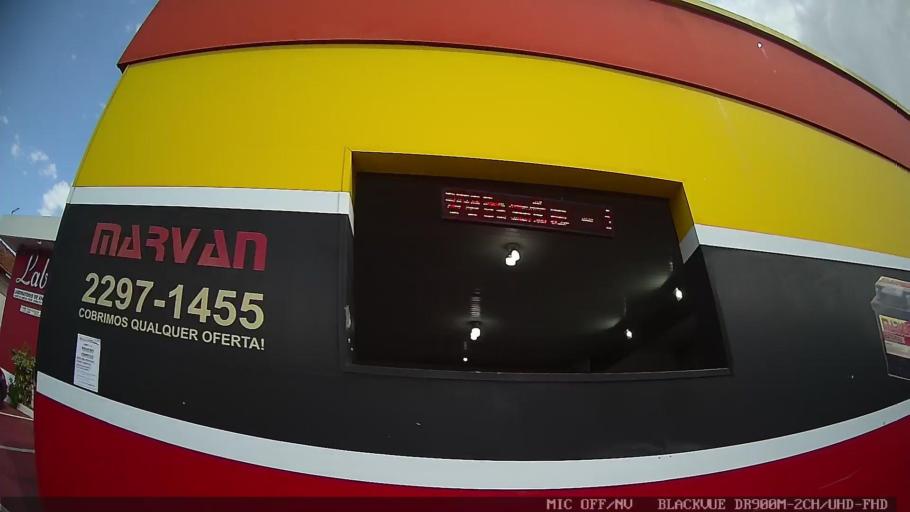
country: BR
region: Sao Paulo
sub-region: Guarulhos
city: Guarulhos
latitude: -23.4922
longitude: -46.4478
